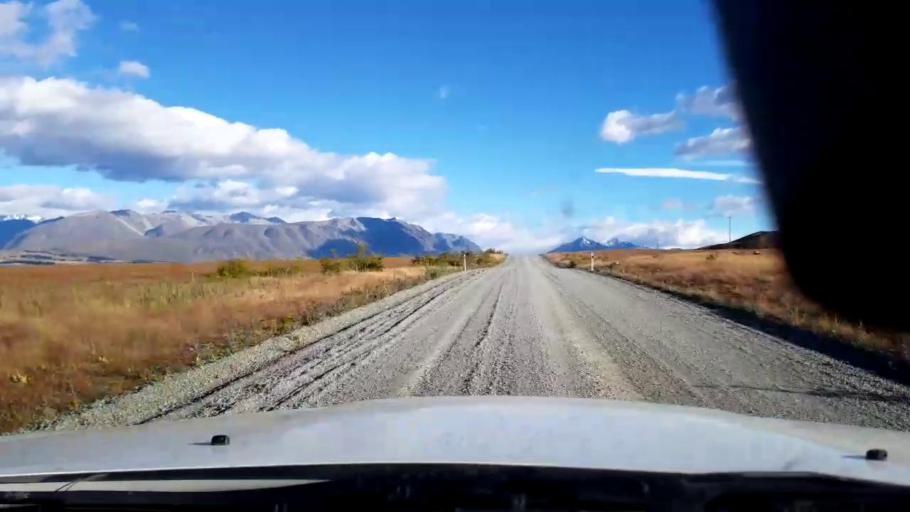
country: NZ
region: Canterbury
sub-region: Timaru District
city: Pleasant Point
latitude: -43.9215
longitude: 170.5595
